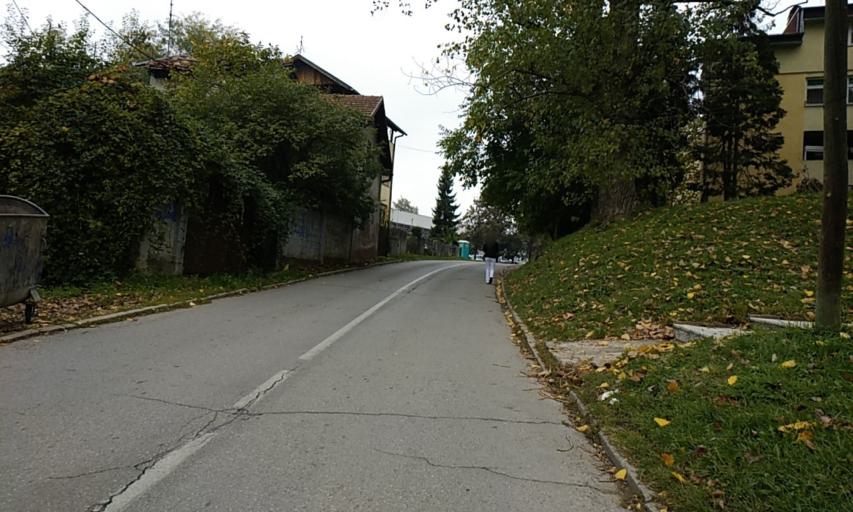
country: BA
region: Republika Srpska
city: Mejdan - Obilicevo
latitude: 44.7676
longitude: 17.1941
